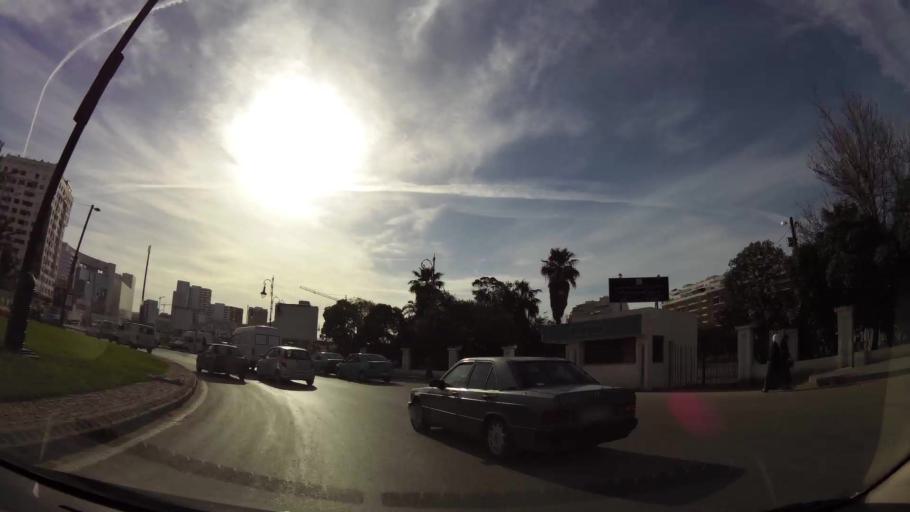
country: MA
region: Tanger-Tetouan
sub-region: Tanger-Assilah
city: Tangier
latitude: 35.7720
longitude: -5.7914
